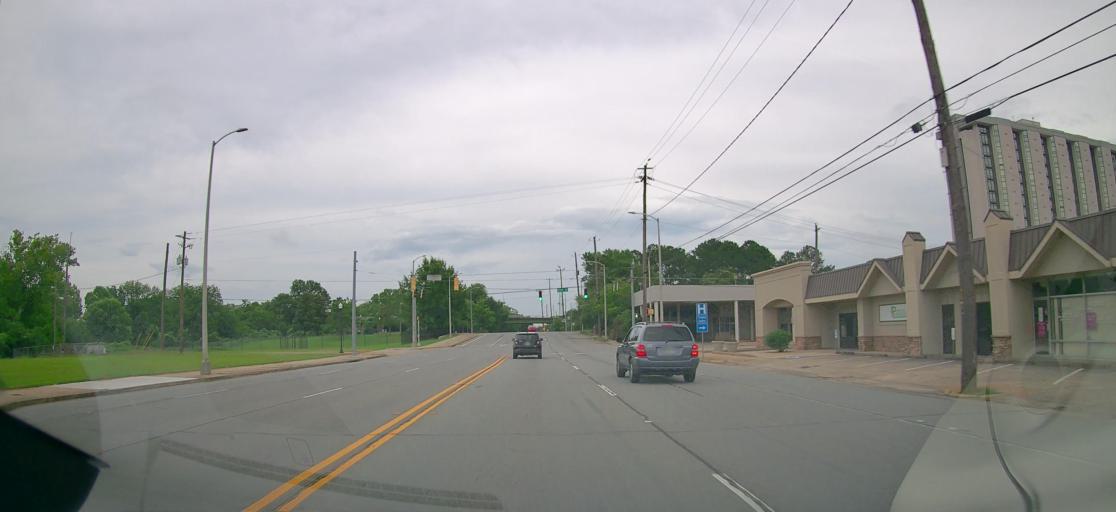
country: US
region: Georgia
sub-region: Bibb County
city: Macon
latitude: 32.8418
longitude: -83.6278
